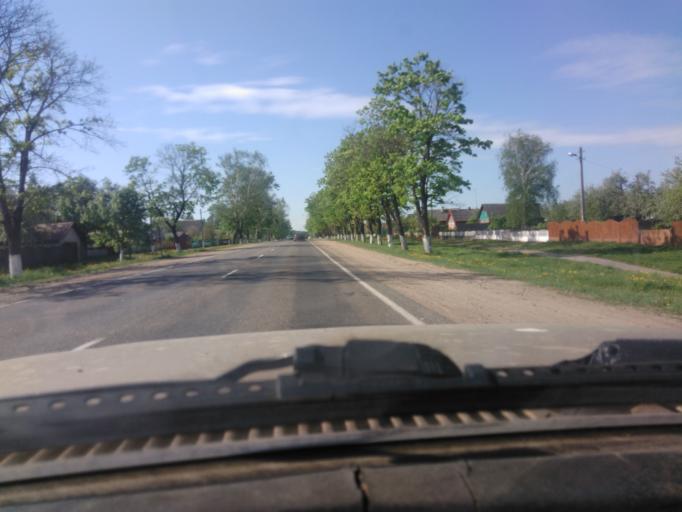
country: BY
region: Mogilev
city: Buynichy
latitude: 53.8273
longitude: 30.2423
